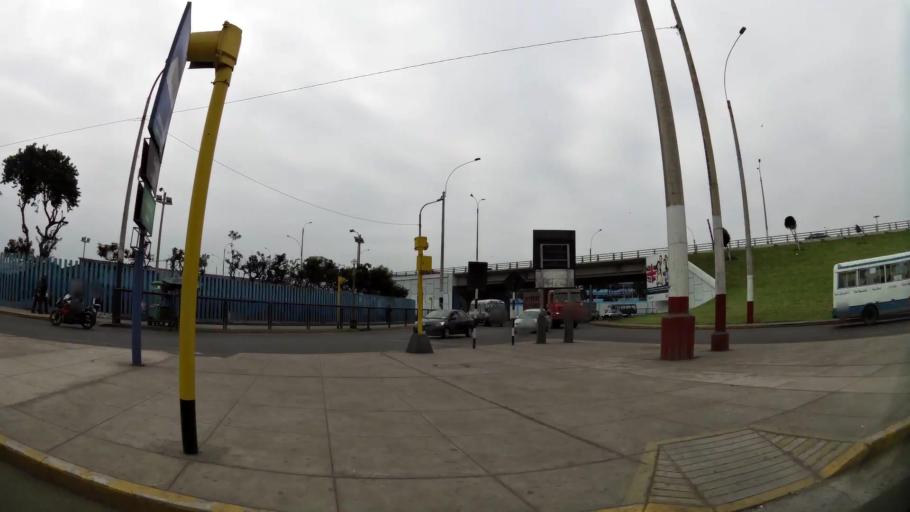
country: PE
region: Callao
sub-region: Callao
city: Callao
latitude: -12.0655
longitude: -77.1200
